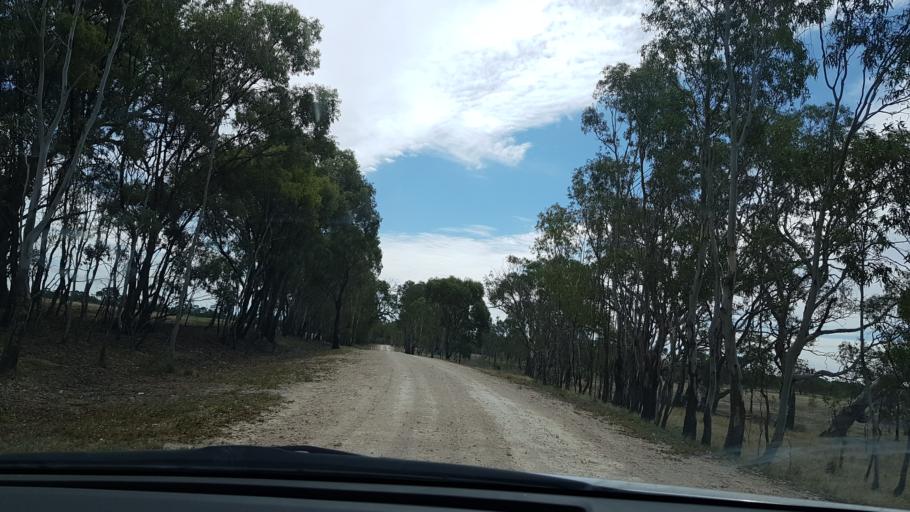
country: AU
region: Victoria
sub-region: Horsham
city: Horsham
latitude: -36.6885
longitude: 141.7831
